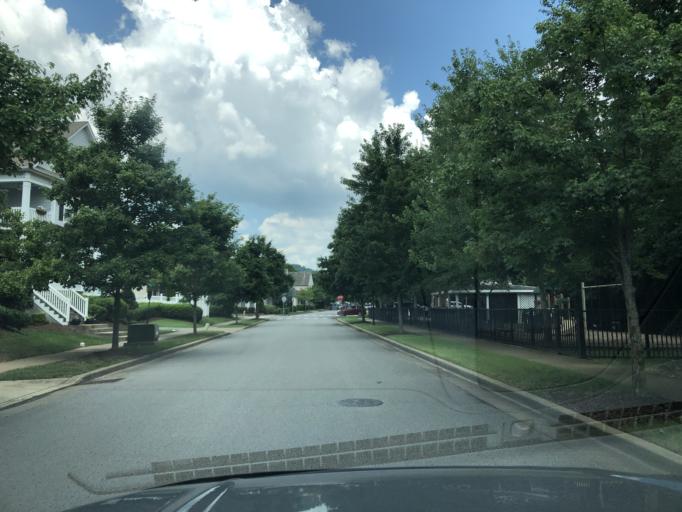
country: US
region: Tennessee
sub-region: Williamson County
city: Brentwood Estates
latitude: 36.0210
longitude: -86.7057
